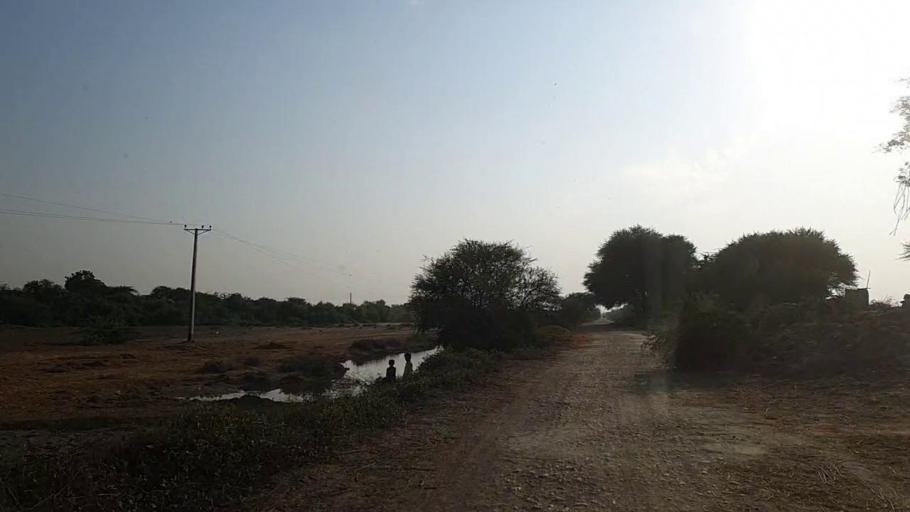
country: PK
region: Sindh
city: Mirpur Batoro
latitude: 24.7741
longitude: 68.2378
